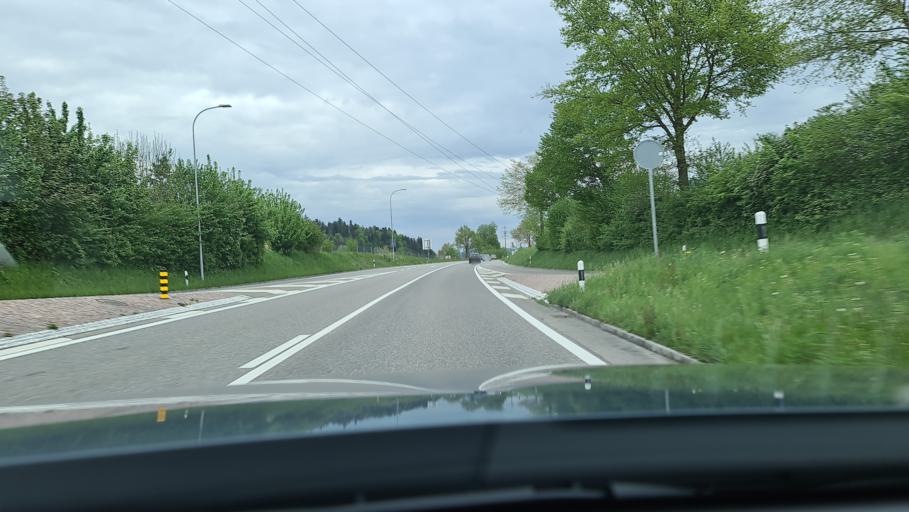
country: CH
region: Aargau
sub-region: Bezirk Kulm
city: Schoftland
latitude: 47.3031
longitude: 8.0430
